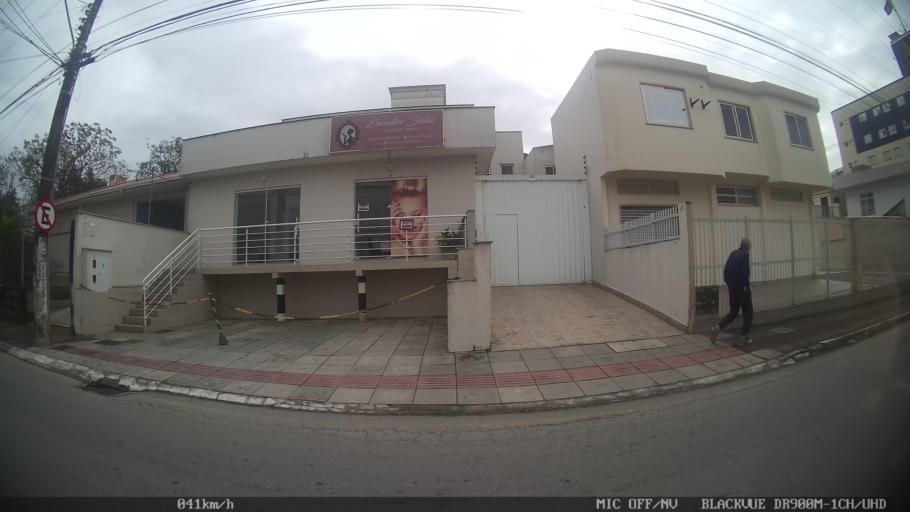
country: BR
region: Santa Catarina
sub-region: Sao Jose
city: Campinas
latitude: -27.5639
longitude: -48.6236
